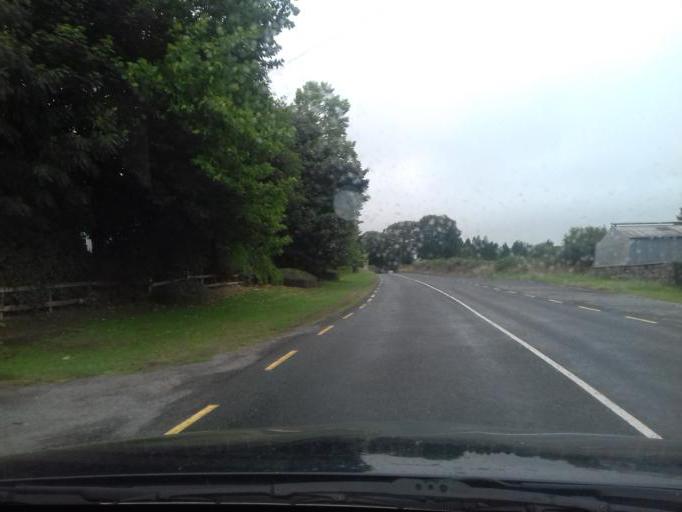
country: IE
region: Leinster
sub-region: Kilkenny
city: Graiguenamanagh
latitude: 52.6165
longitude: -6.9371
